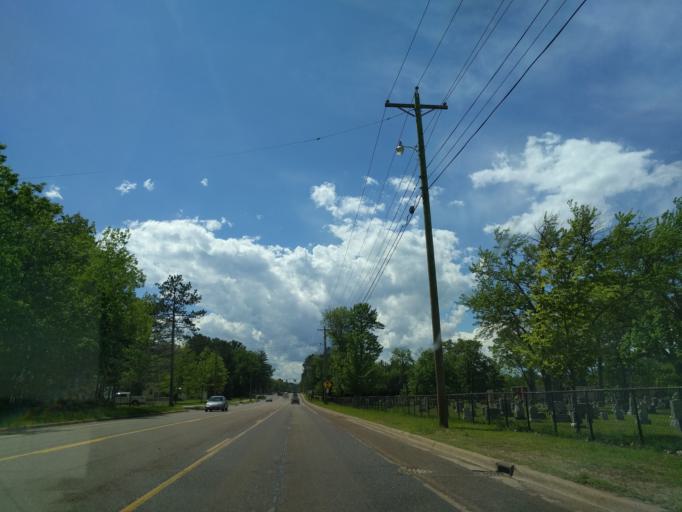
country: US
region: Michigan
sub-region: Marquette County
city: Trowbridge Park
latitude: 46.5640
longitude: -87.4171
